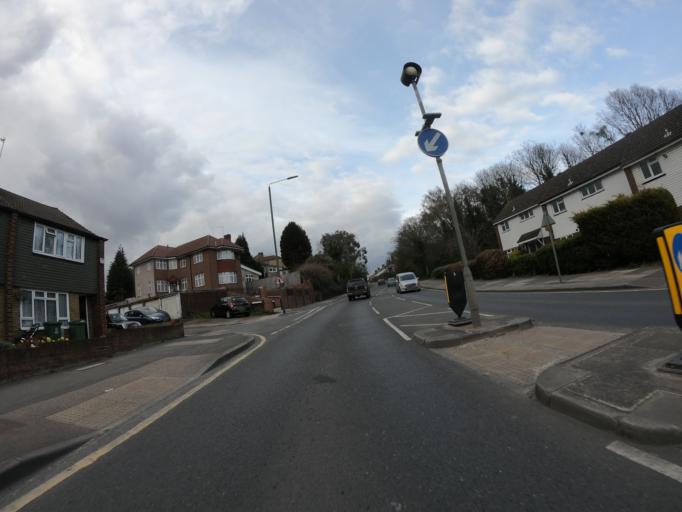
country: GB
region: England
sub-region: Greater London
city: Bexleyheath
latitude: 51.4687
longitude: 0.1587
